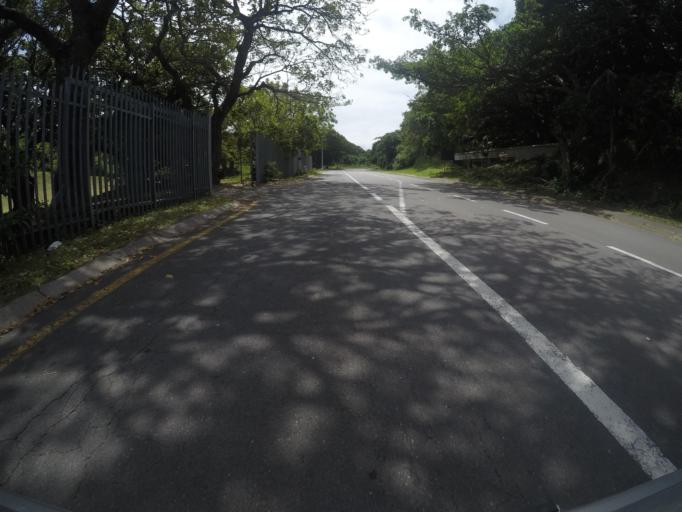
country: ZA
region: Eastern Cape
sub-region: Buffalo City Metropolitan Municipality
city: East London
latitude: -33.0223
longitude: 27.9090
